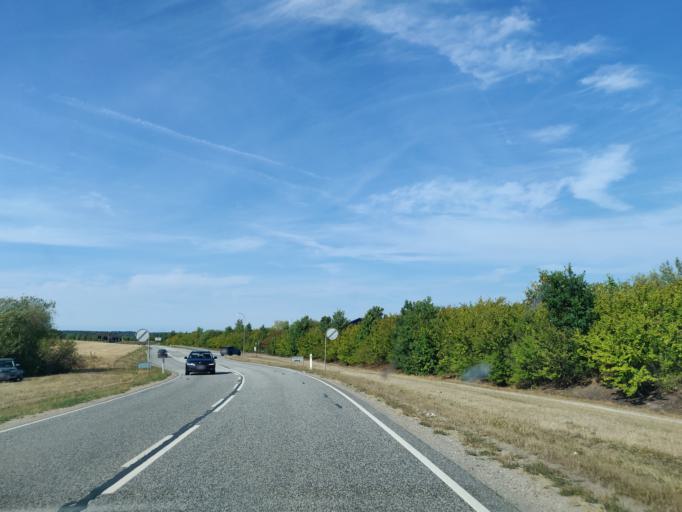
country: DK
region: Zealand
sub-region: Roskilde Kommune
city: Svogerslev
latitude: 55.6314
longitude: 12.0434
